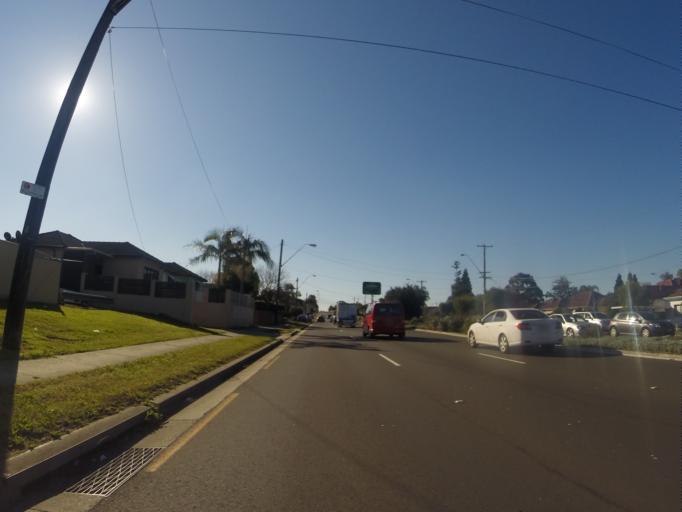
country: AU
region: New South Wales
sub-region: Canterbury
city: Lakemba
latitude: -33.9143
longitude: 151.0629
